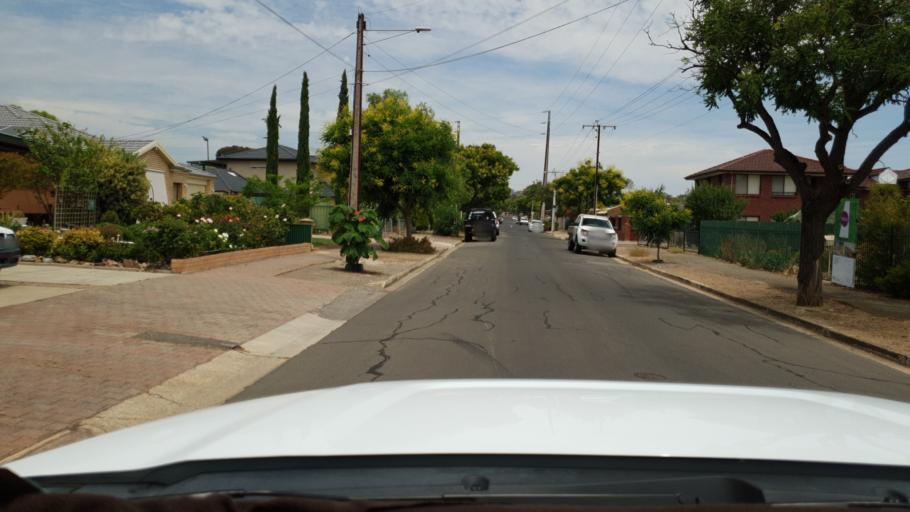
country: AU
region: South Australia
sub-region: Marion
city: Clovelly Park
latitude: -34.9949
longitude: 138.5811
